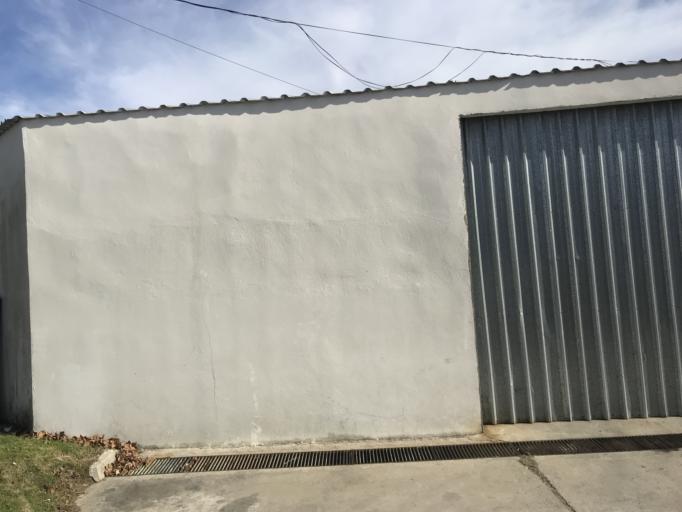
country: UY
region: Colonia
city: Colonia del Sacramento
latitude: -34.4720
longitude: -57.8417
